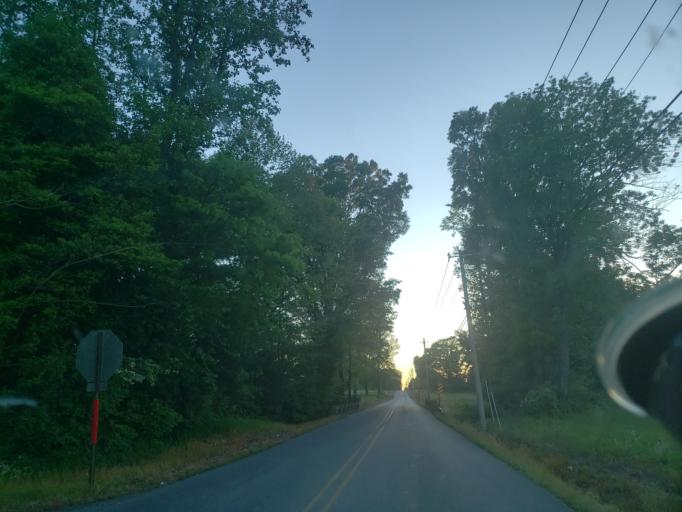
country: US
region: Alabama
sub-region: Madison County
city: Hazel Green
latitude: 34.9770
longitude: -86.6416
